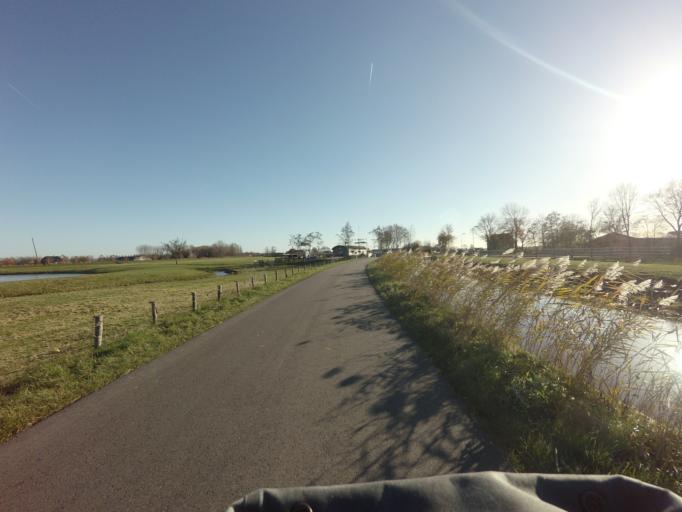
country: NL
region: North Holland
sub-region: Gemeente Amsterdam
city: Amsterdam-Zuidoost
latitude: 52.2625
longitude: 4.9731
